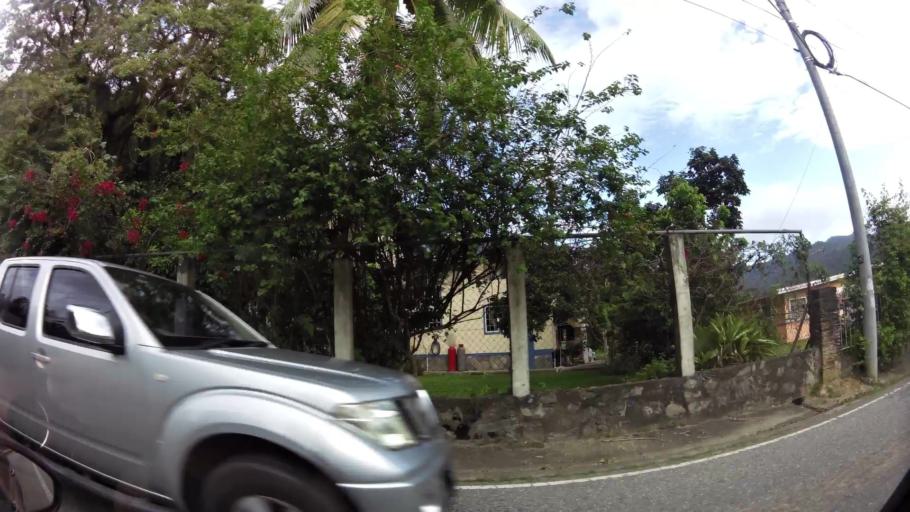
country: TT
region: Diego Martin
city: Petit Valley
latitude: 10.7164
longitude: -61.4730
